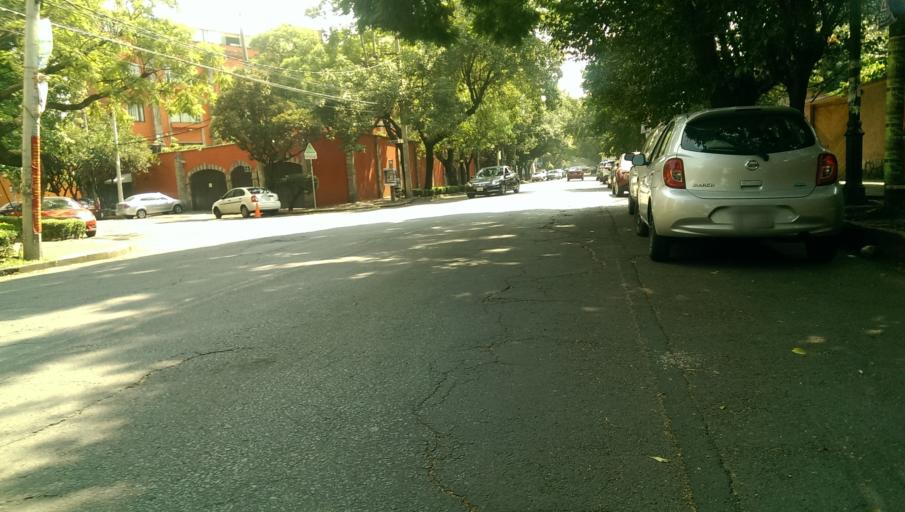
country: MX
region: Mexico City
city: Coyoacan
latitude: 19.3549
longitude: -99.1677
